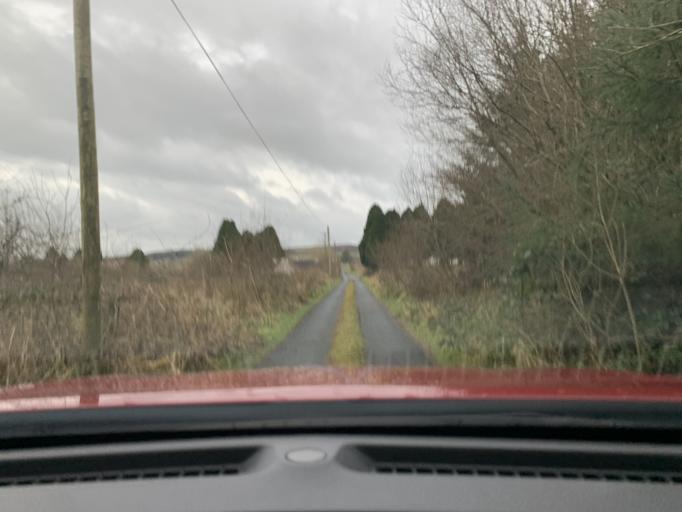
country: IE
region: Connaught
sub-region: Roscommon
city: Ballaghaderreen
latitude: 53.9644
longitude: -8.5042
